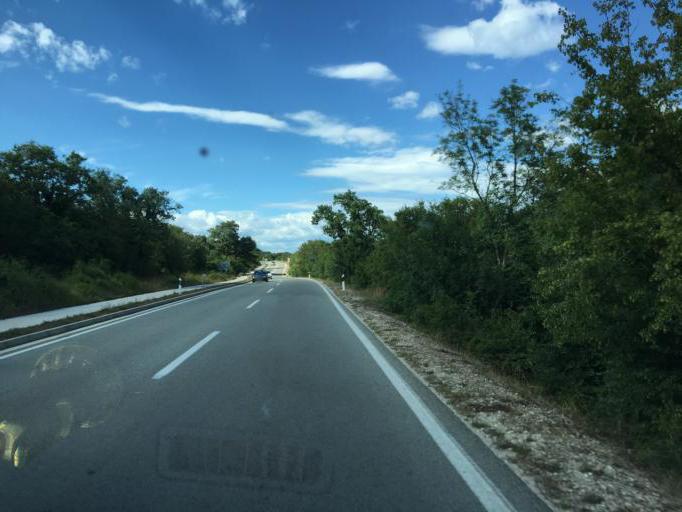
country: HR
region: Primorsko-Goranska
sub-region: Grad Krk
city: Krk
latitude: 45.0612
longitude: 14.5561
